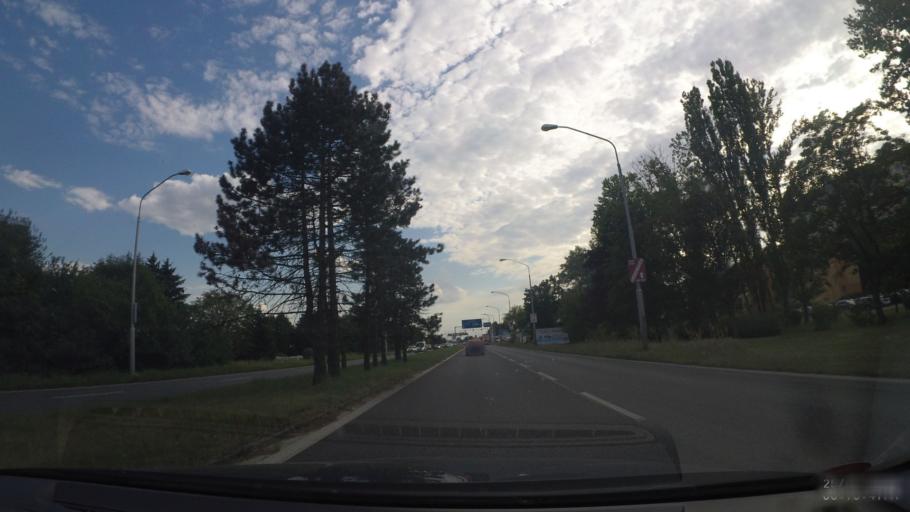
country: CZ
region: Kralovehradecky
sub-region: Okres Hradec Kralove
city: Hradec Kralove
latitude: 50.1980
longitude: 15.8160
